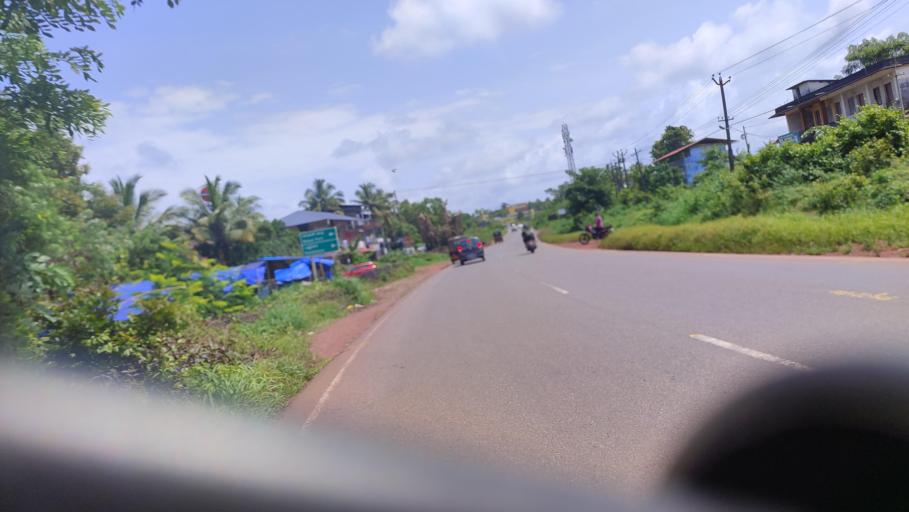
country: IN
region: Kerala
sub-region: Kasaragod District
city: Kannangad
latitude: 12.4033
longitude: 75.0965
